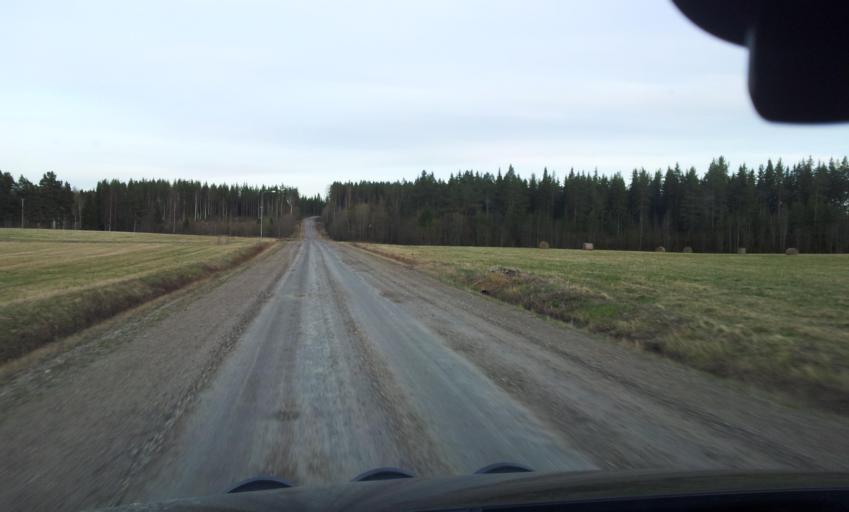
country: SE
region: Gaevleborg
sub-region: Ljusdals Kommun
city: Farila
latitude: 62.0537
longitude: 15.8132
